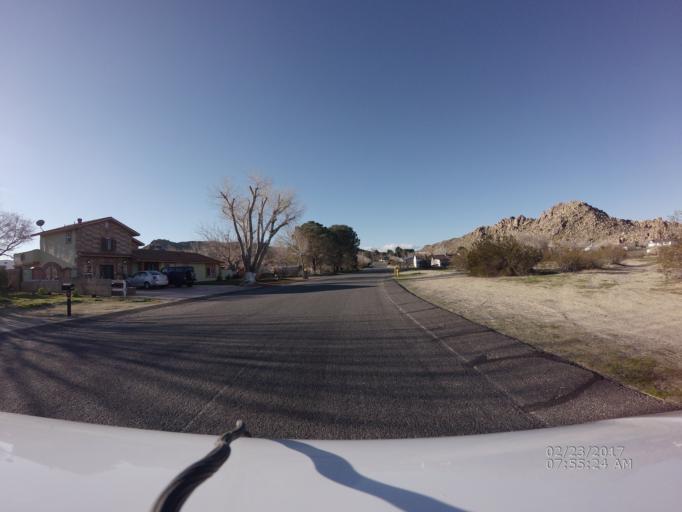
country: US
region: California
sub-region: Los Angeles County
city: Lake Los Angeles
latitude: 34.6118
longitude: -117.8172
